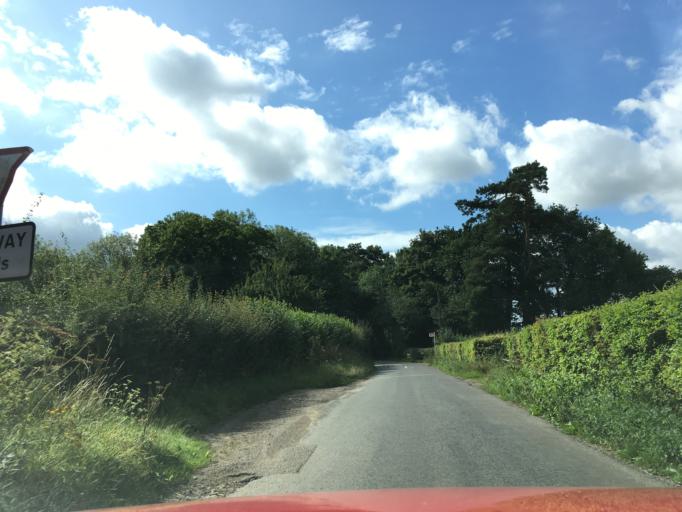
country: GB
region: England
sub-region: Kent
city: Maidstone
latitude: 51.2264
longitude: 0.5512
